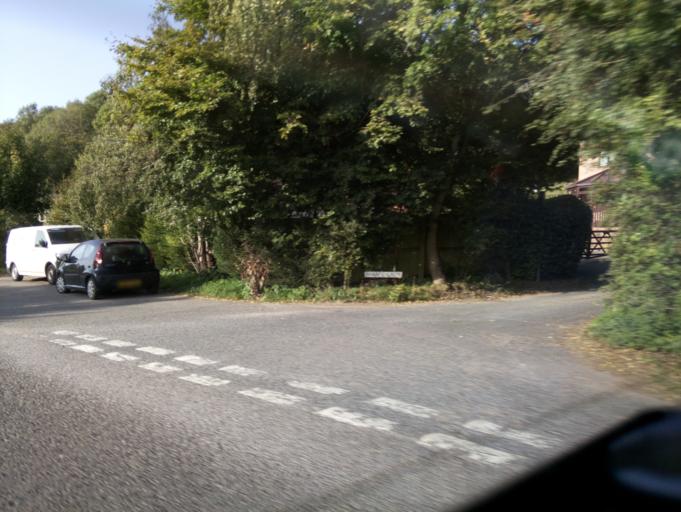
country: GB
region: England
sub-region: Gloucestershire
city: Gloucester
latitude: 51.9065
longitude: -2.2923
